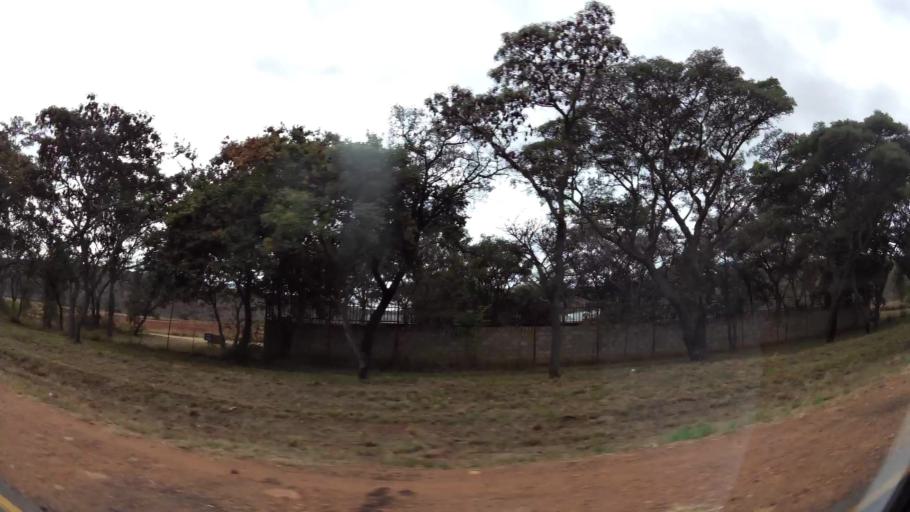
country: ZA
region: Limpopo
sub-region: Waterberg District Municipality
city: Modimolle
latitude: -24.6780
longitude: 28.5243
